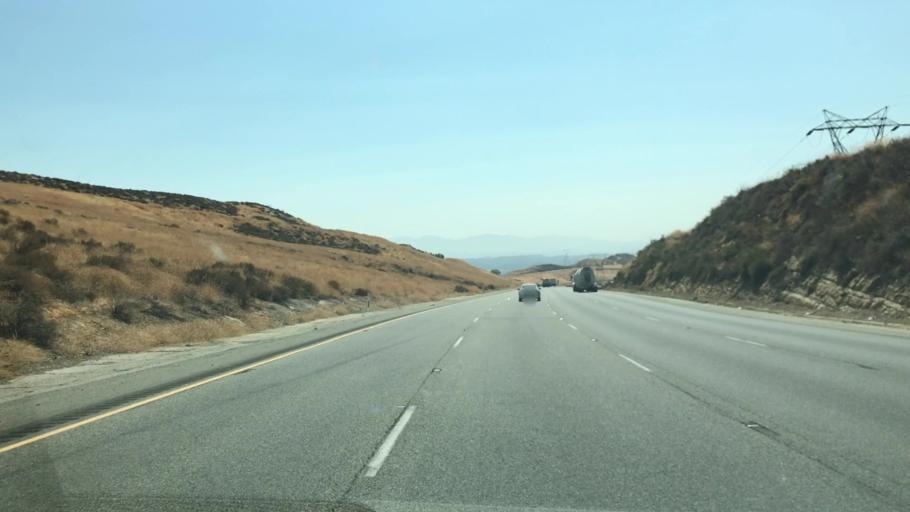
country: US
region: California
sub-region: Los Angeles County
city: Castaic
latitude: 34.5430
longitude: -118.6524
